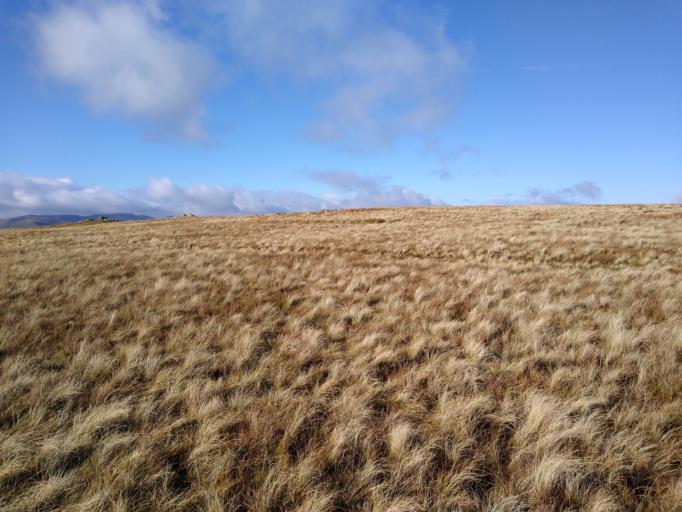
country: GB
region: England
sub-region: Cumbria
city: Ambleside
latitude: 54.5070
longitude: -2.8615
